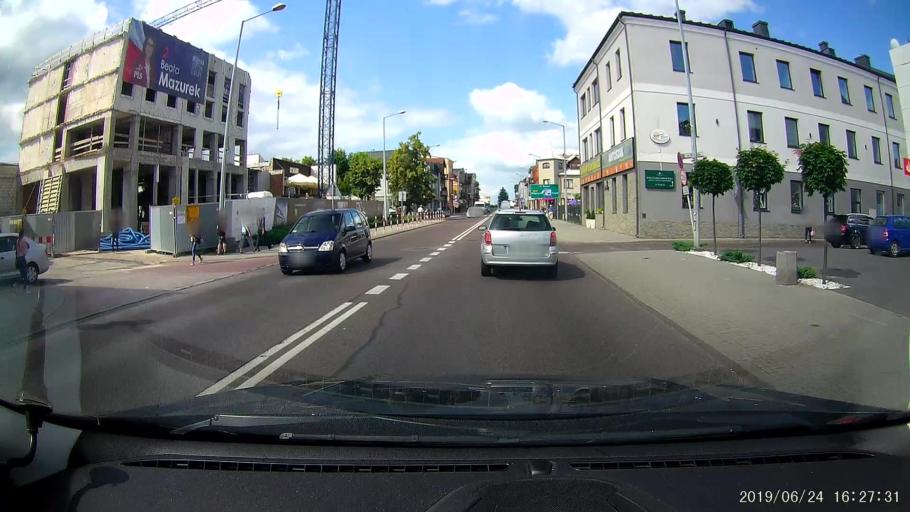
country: PL
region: Lublin Voivodeship
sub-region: Powiat tomaszowski
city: Tomaszow Lubelski
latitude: 50.4510
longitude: 23.4180
